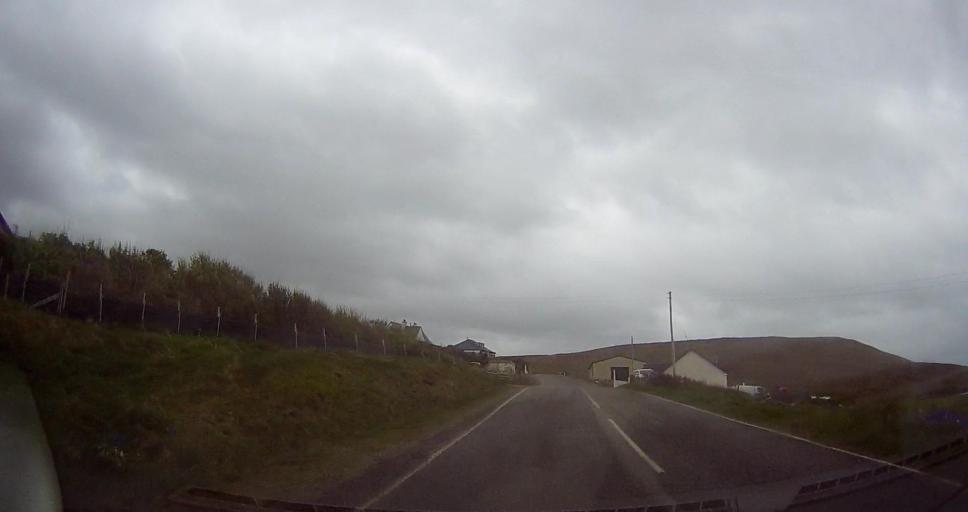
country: GB
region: Scotland
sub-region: Shetland Islands
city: Lerwick
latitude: 60.4906
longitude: -1.4522
